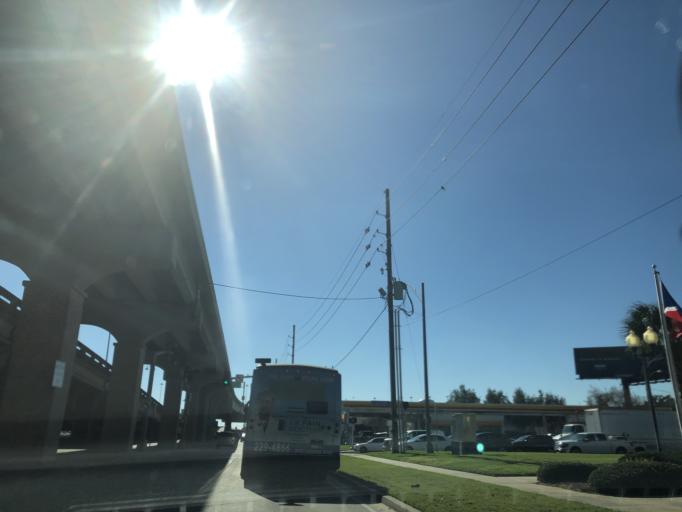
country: US
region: Louisiana
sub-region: Jefferson Parish
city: Metairie
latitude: 30.0034
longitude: -90.1554
